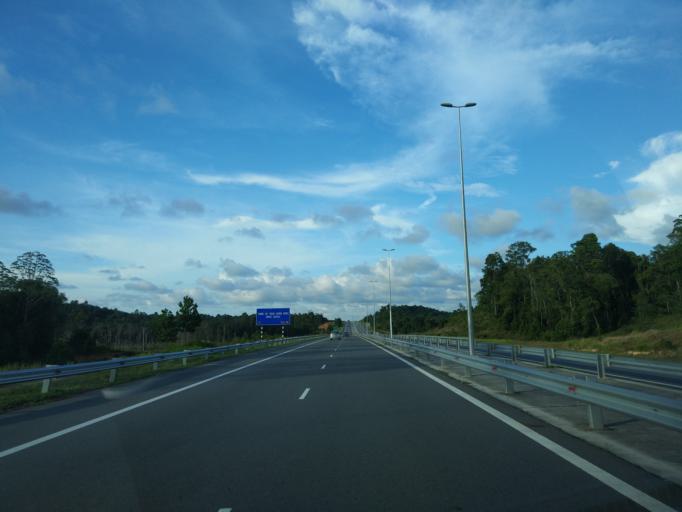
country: BN
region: Tutong
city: Tutong
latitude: 4.7017
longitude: 114.5714
